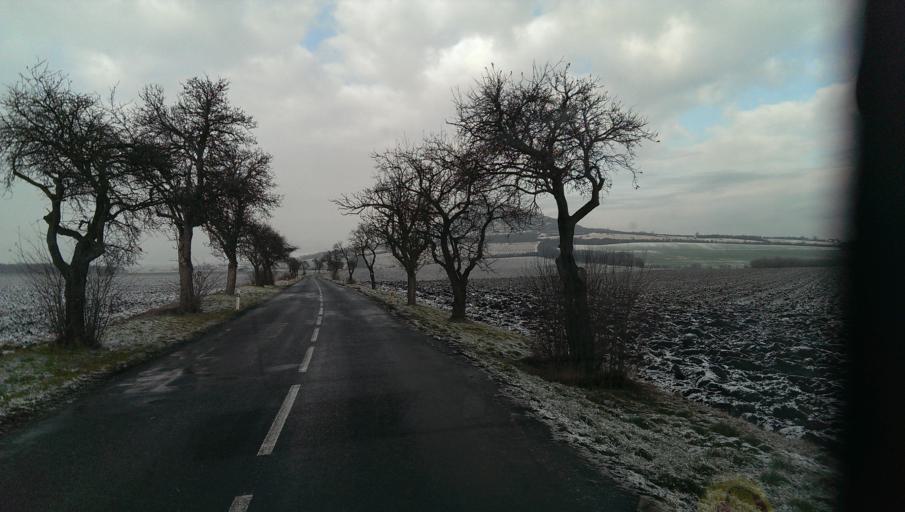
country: CZ
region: Ustecky
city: Libochovice
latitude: 50.4136
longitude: 14.0294
